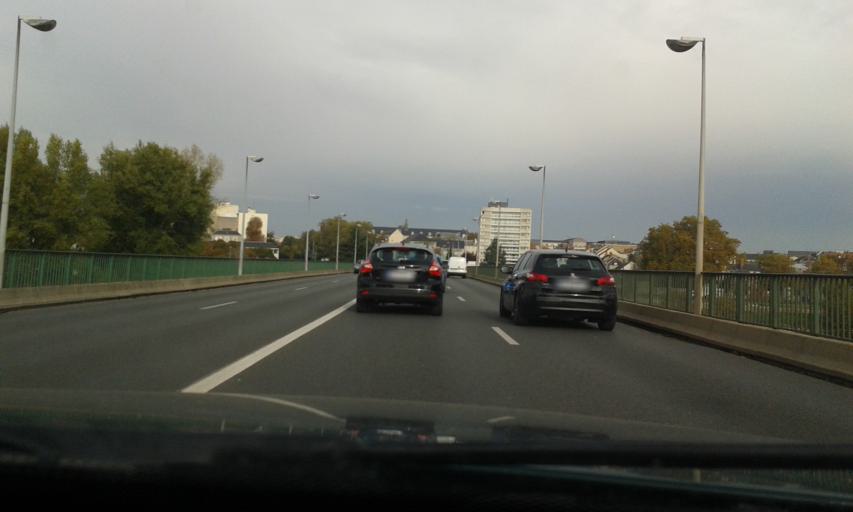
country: FR
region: Centre
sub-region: Departement du Loiret
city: Orleans
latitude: 47.8954
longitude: 1.8956
